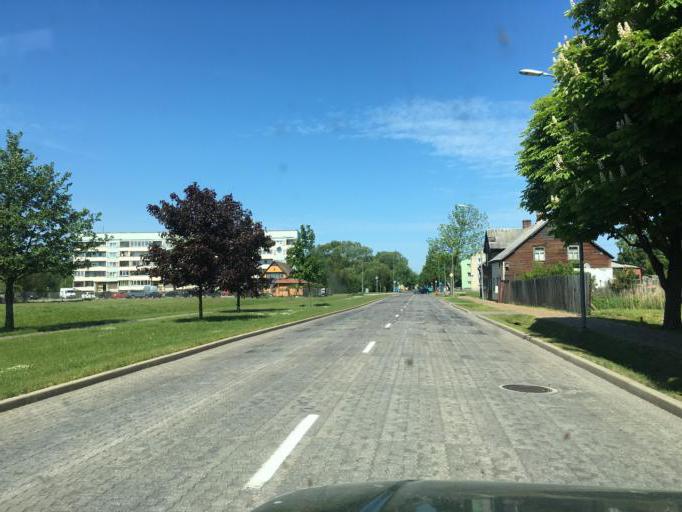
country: LV
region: Ventspils
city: Ventspils
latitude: 57.3978
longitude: 21.6091
